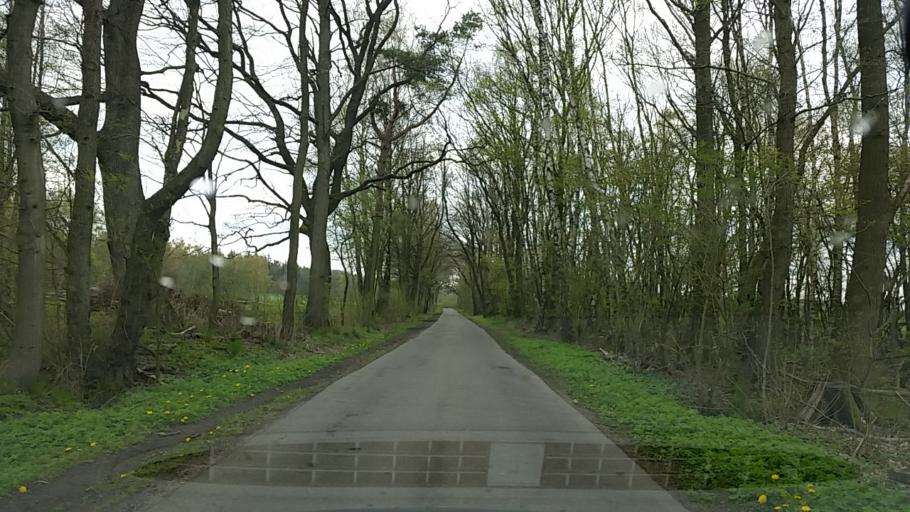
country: DE
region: Schleswig-Holstein
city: Rausdorf
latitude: 53.5628
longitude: 10.2949
